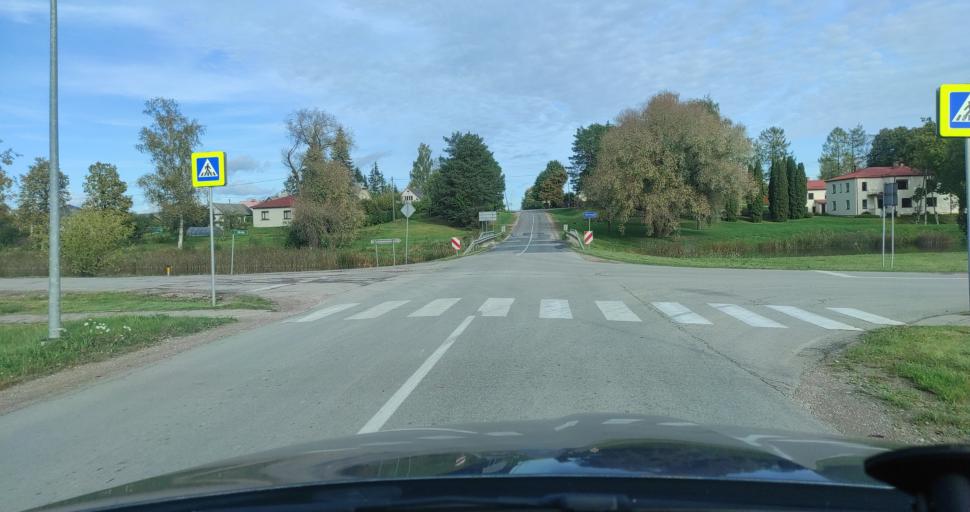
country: LV
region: Jaunpils
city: Jaunpils
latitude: 56.7312
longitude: 23.0124
